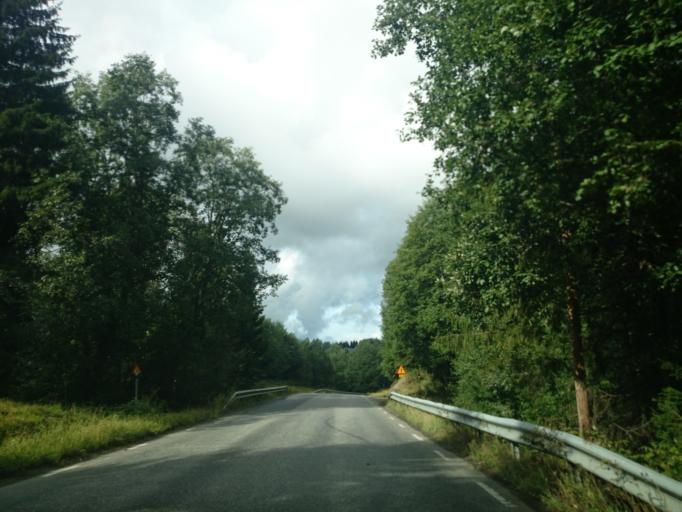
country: SE
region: Vaesternorrland
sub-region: Sundsvalls Kommun
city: Vi
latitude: 62.3100
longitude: 17.2178
